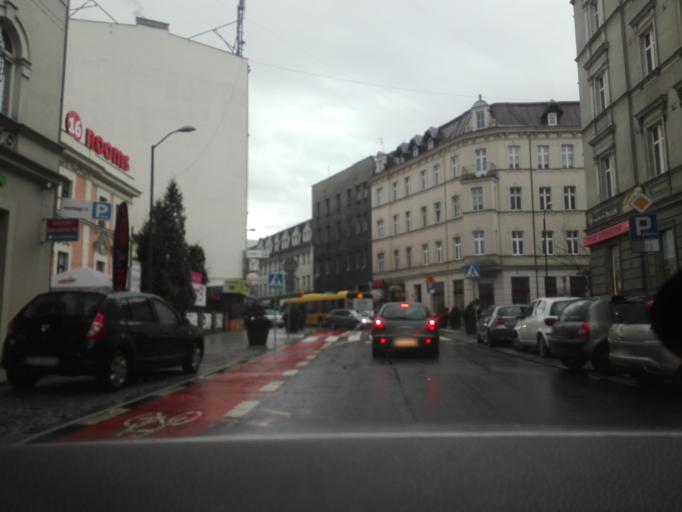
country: PL
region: Silesian Voivodeship
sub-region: Katowice
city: Katowice
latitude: 50.2608
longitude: 19.0161
